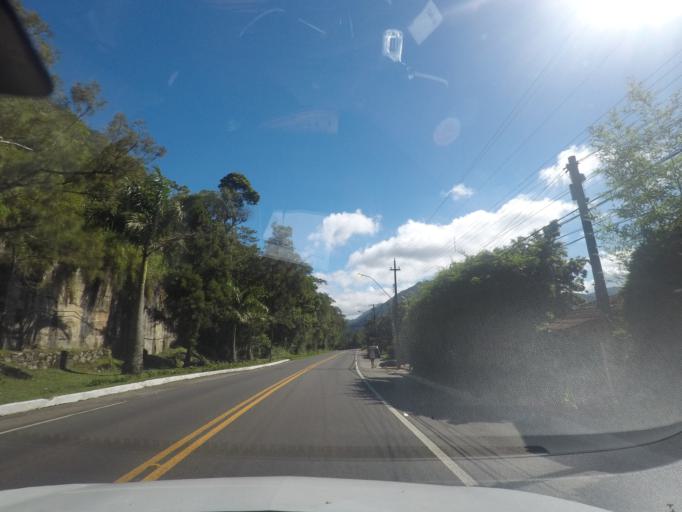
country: BR
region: Rio de Janeiro
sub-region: Teresopolis
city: Teresopolis
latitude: -22.4593
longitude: -42.9873
